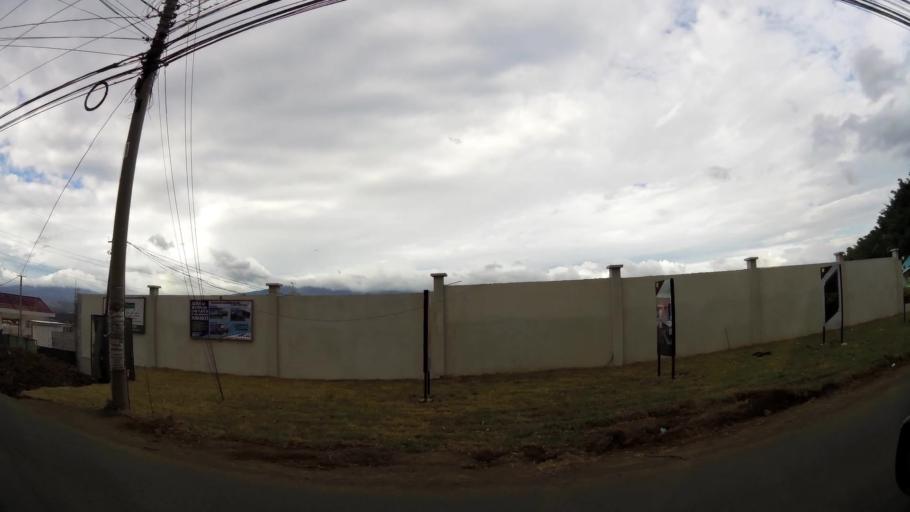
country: CR
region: Heredia
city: La Asuncion
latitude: 9.9599
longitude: -84.1723
